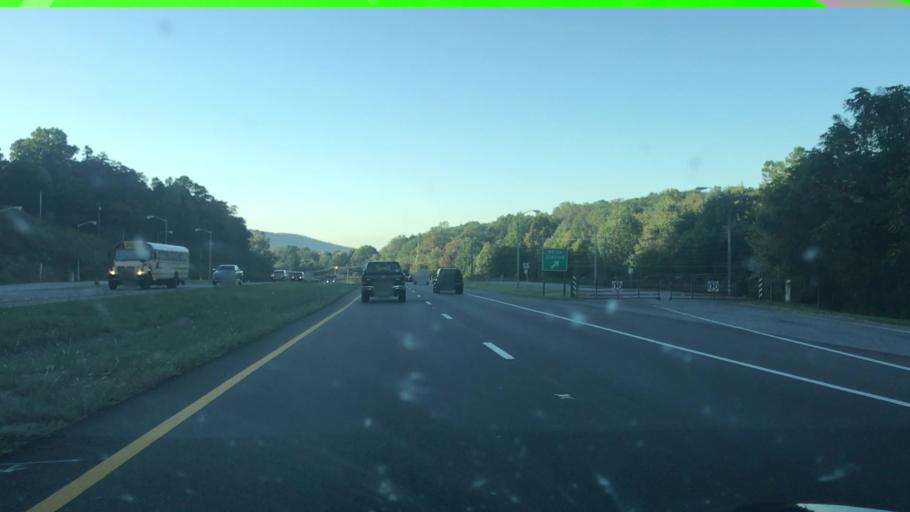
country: US
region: Virginia
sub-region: Botetourt County
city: Cloverdale
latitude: 37.3492
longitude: -79.8831
